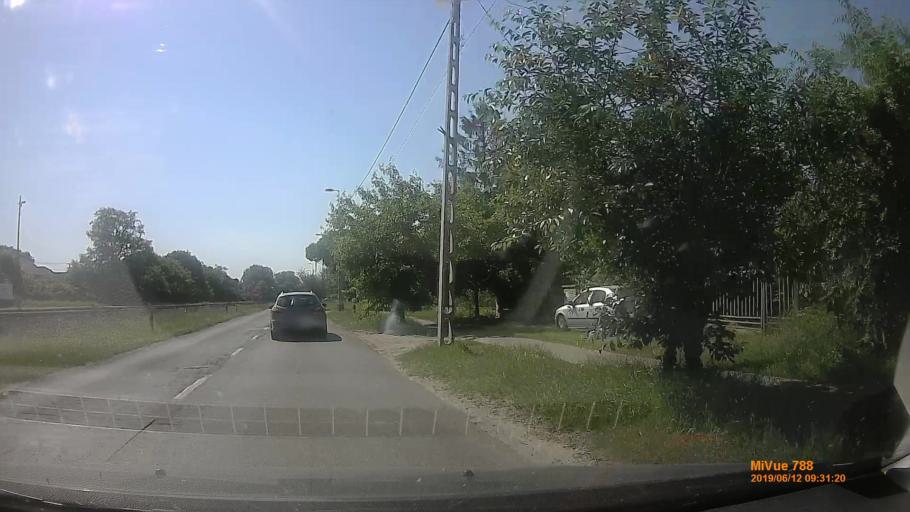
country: HU
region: Pest
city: Gyal
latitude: 47.4017
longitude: 19.1889
